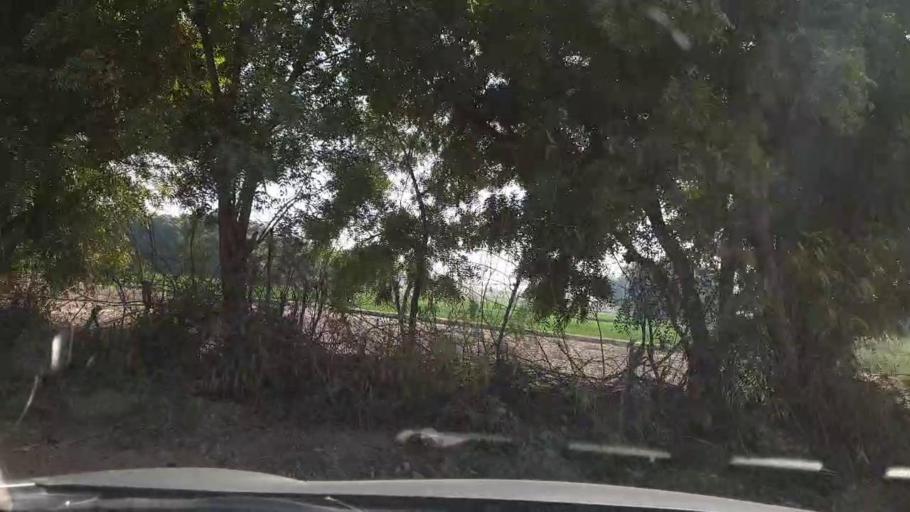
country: PK
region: Sindh
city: Tando Allahyar
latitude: 25.4681
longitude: 68.6443
